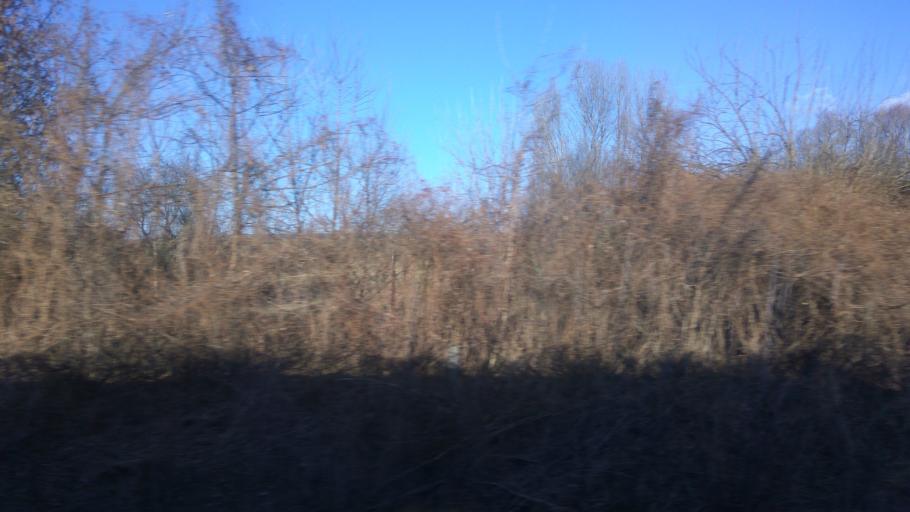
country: HU
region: Pest
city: Pecel
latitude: 47.4952
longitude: 19.3157
